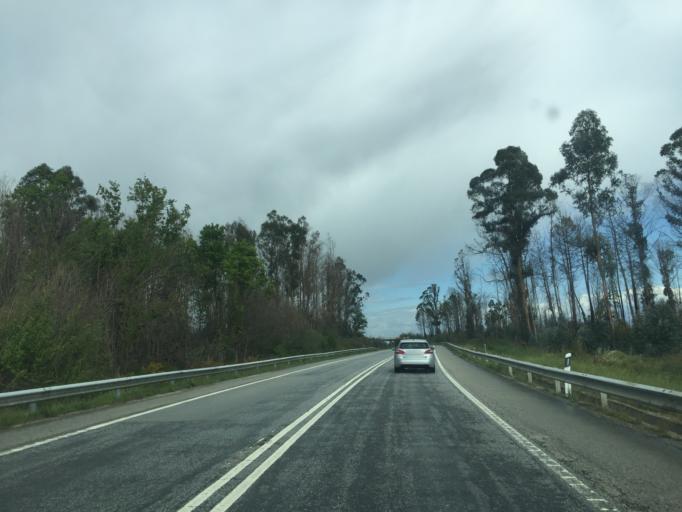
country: PT
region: Viseu
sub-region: Viseu
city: Abraveses
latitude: 40.6549
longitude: -8.0260
